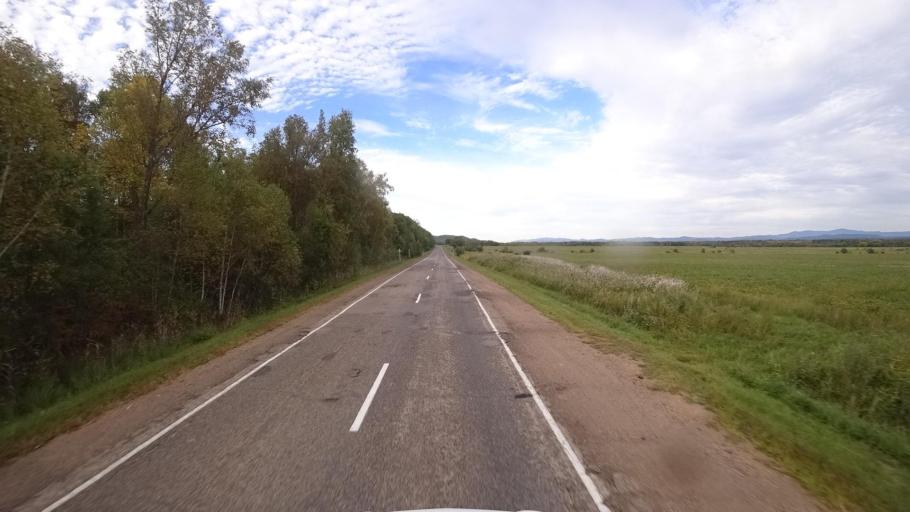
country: RU
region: Primorskiy
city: Dostoyevka
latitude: 44.3557
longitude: 133.4266
